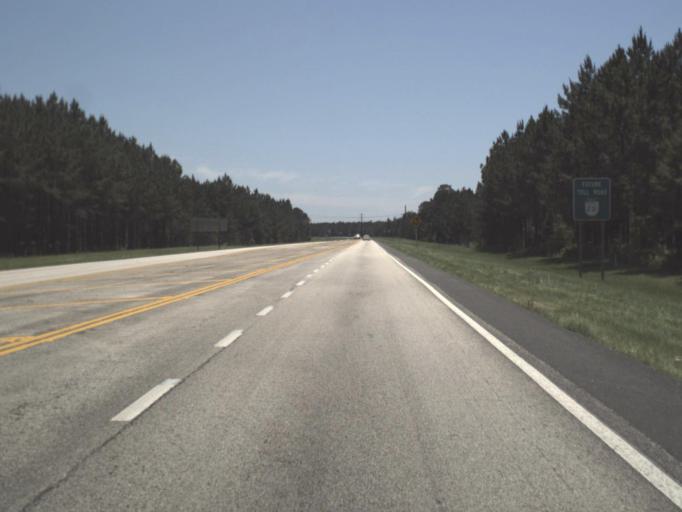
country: US
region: Florida
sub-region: Clay County
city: Lakeside
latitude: 30.1941
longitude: -81.8376
